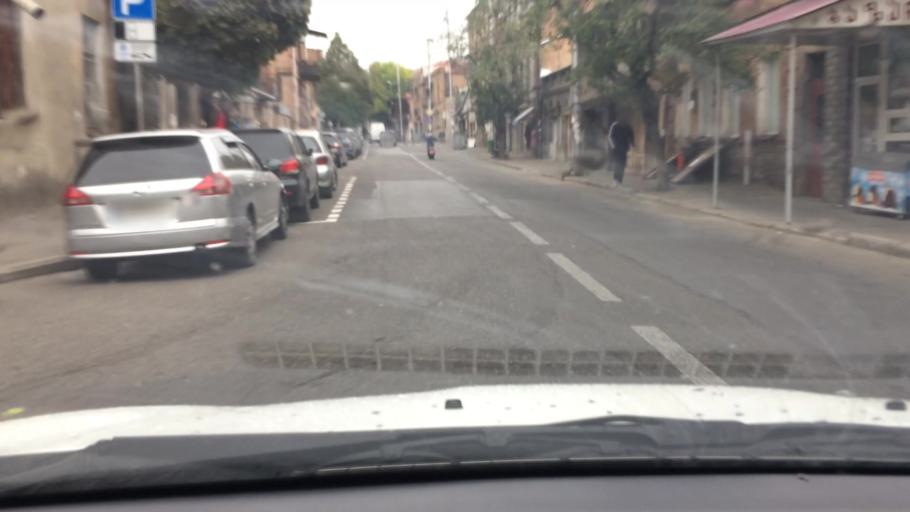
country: GE
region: T'bilisi
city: Tbilisi
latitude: 41.7062
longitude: 44.8056
